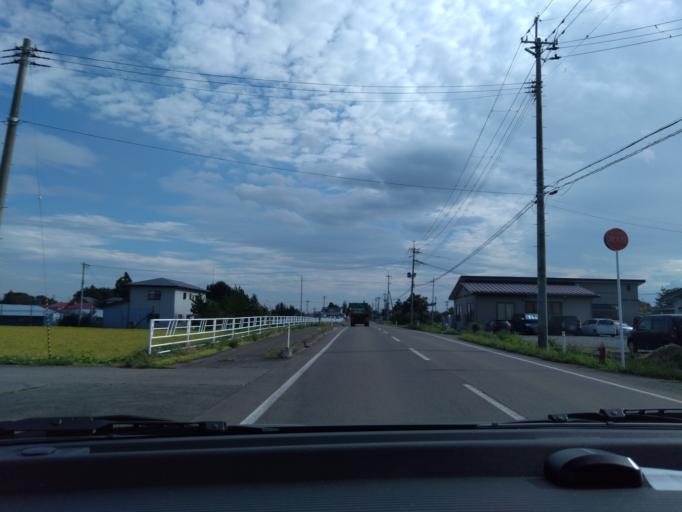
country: JP
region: Iwate
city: Hanamaki
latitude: 39.4498
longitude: 141.0977
